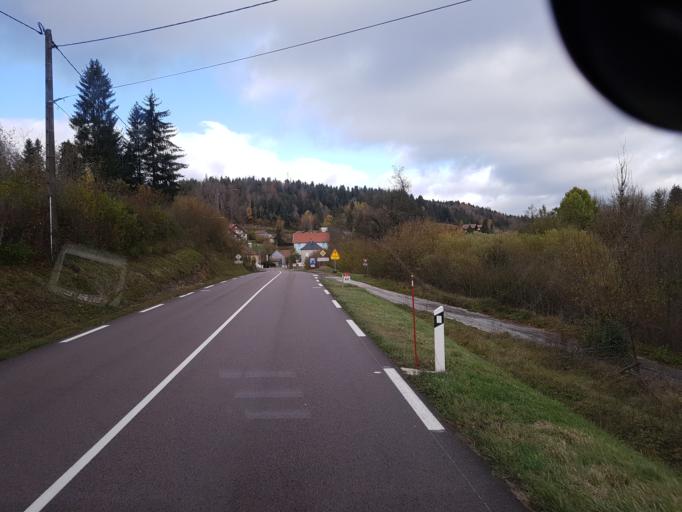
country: FR
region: Franche-Comte
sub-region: Departement du Jura
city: Champagnole
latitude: 46.6523
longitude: 5.9419
